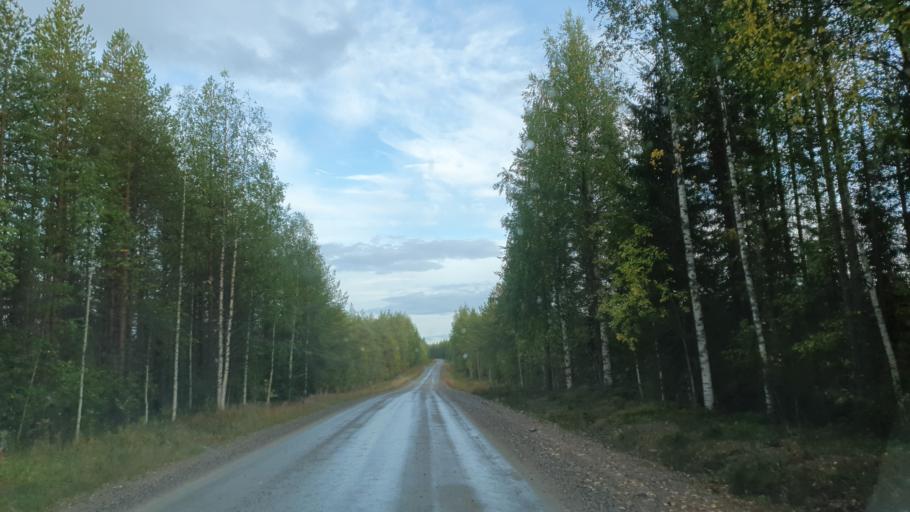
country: FI
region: Kainuu
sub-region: Kehys-Kainuu
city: Kuhmo
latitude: 64.4184
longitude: 29.4965
